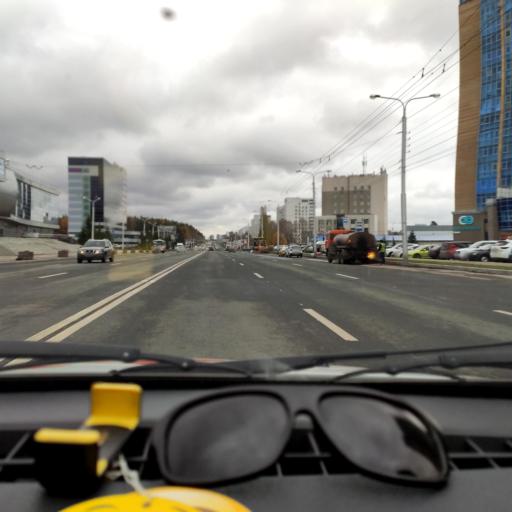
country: RU
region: Bashkortostan
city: Ufa
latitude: 54.7527
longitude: 56.0319
